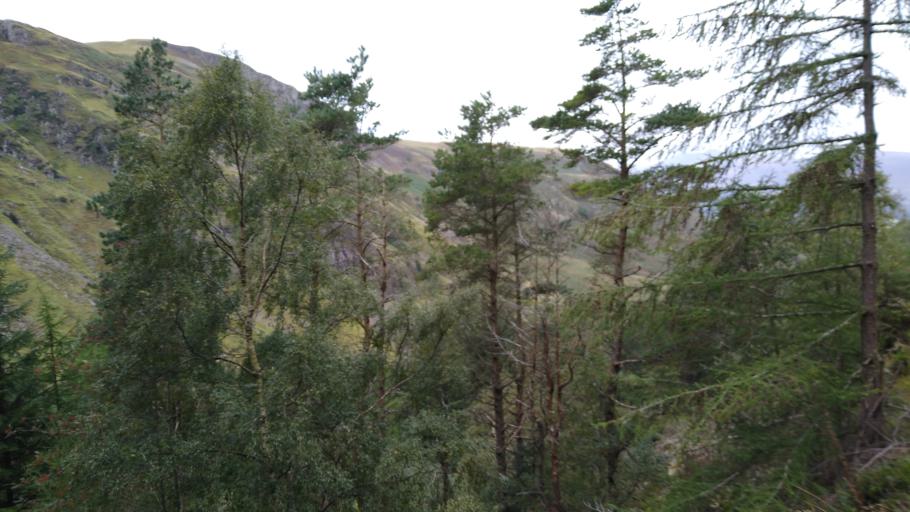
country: GB
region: England
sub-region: Cumbria
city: Keswick
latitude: 54.5641
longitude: -3.0838
